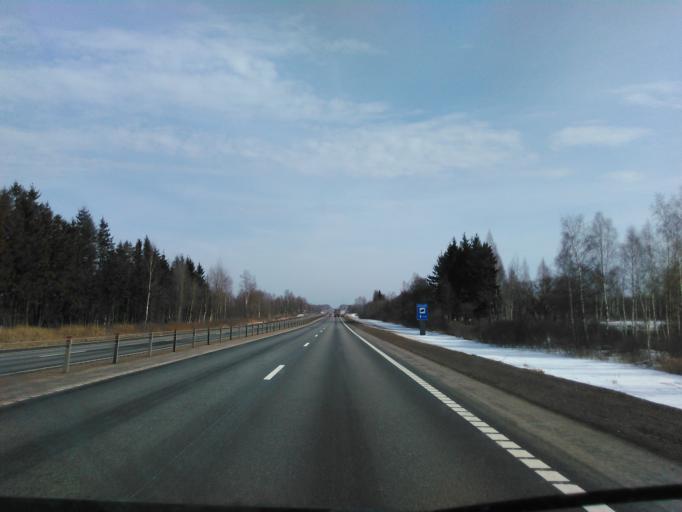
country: BY
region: Vitebsk
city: Dubrowna
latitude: 54.6898
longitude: 30.9231
